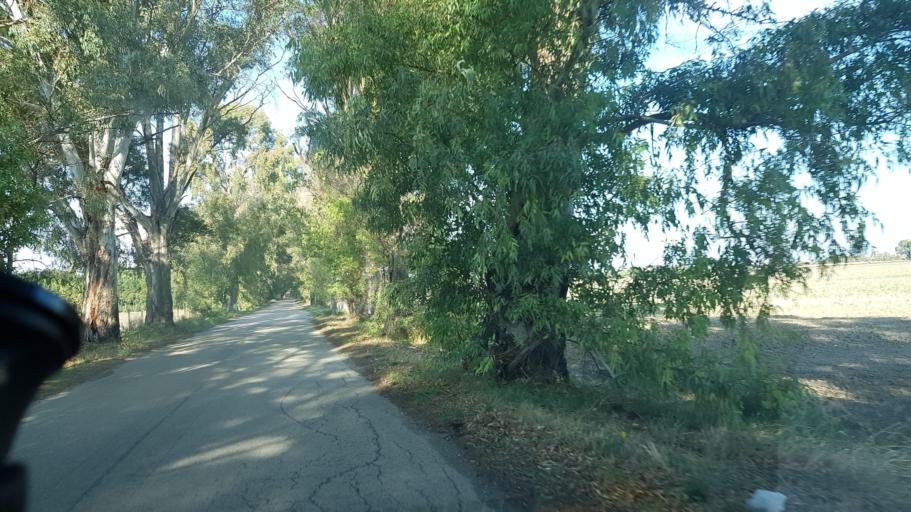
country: IT
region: Apulia
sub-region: Provincia di Foggia
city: Carapelle
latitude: 41.3912
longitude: 15.6509
